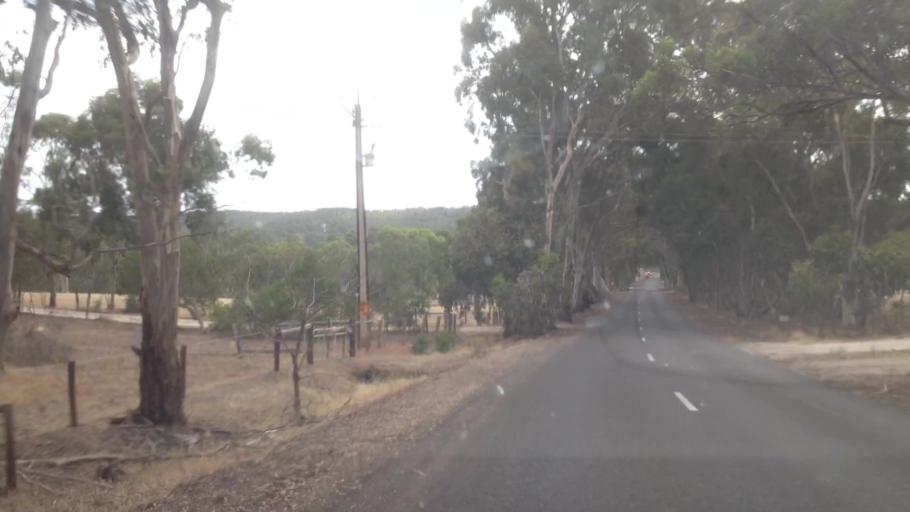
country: AU
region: South Australia
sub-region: Barossa
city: Williamstown
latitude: -34.6423
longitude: 138.8542
